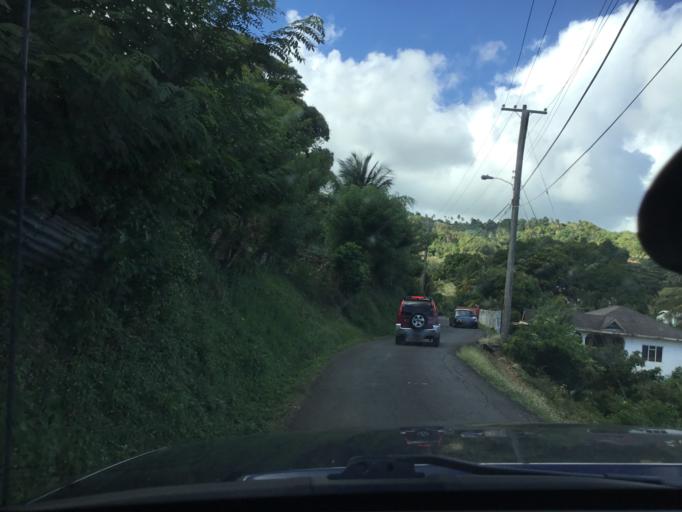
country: VC
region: Saint George
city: Kingstown
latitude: 13.1441
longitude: -61.1741
